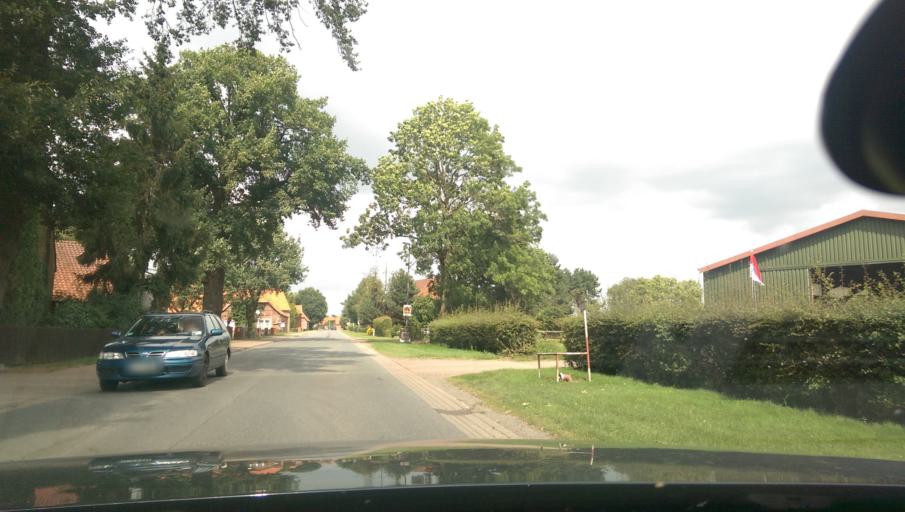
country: DE
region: Lower Saxony
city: Steimbke
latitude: 52.6845
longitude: 9.4810
